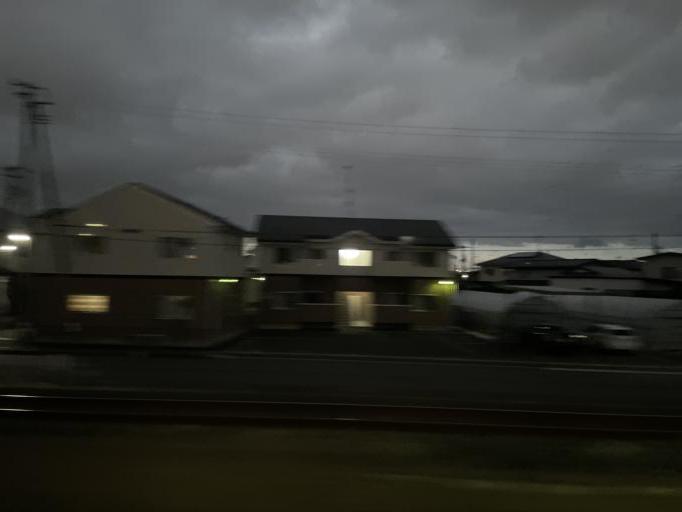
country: JP
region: Aomori
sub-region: Hachinohe Shi
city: Uchimaru
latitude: 40.5222
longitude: 141.4716
